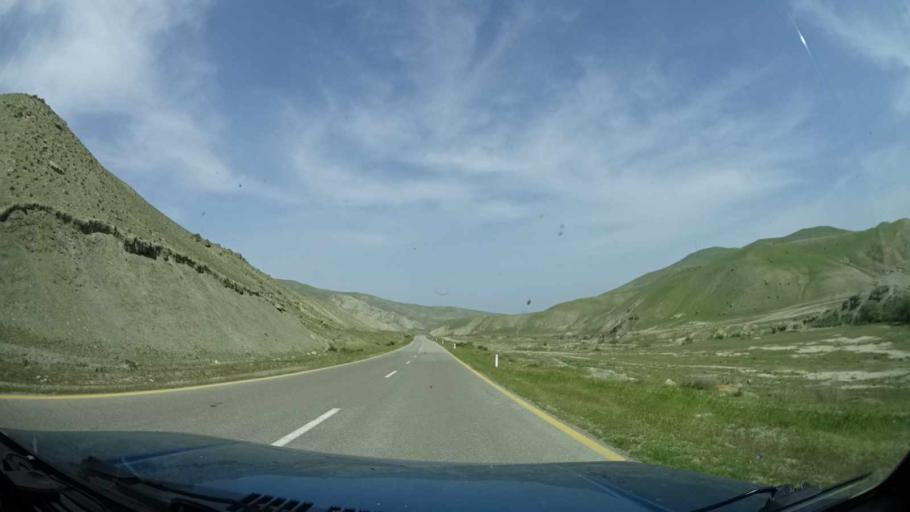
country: AZ
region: Xizi
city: Kilyazi
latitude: 40.8496
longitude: 49.2643
